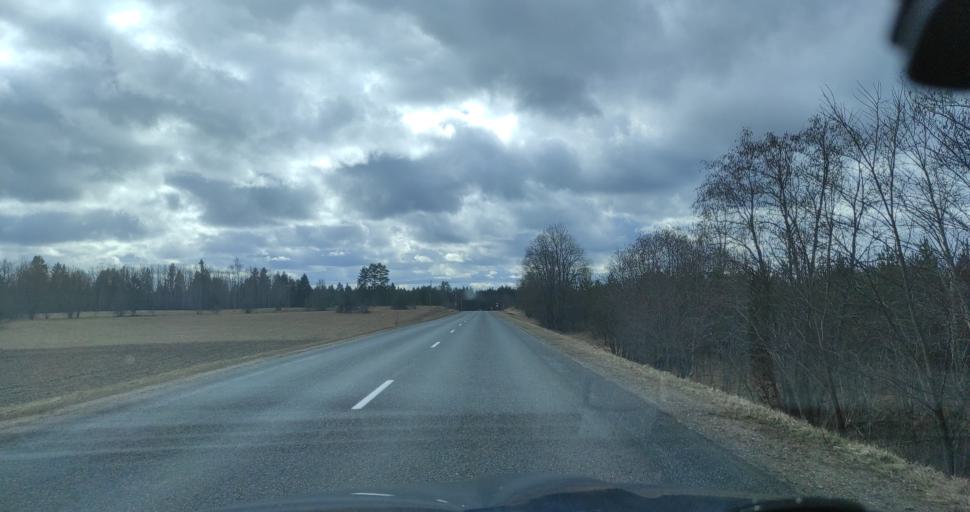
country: LV
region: Talsu Rajons
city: Stende
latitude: 57.0883
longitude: 22.4757
